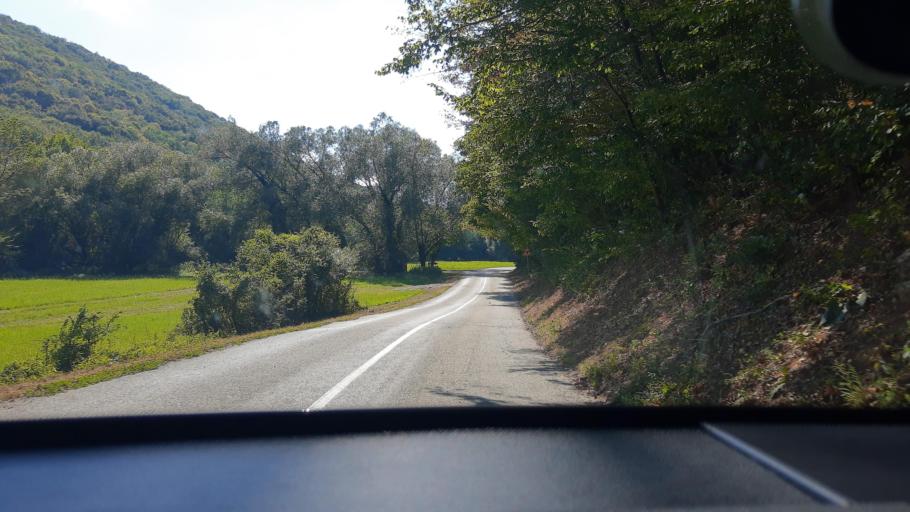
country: SK
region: Trnavsky
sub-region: Okres Trnava
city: Piestany
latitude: 48.6360
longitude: 17.9257
